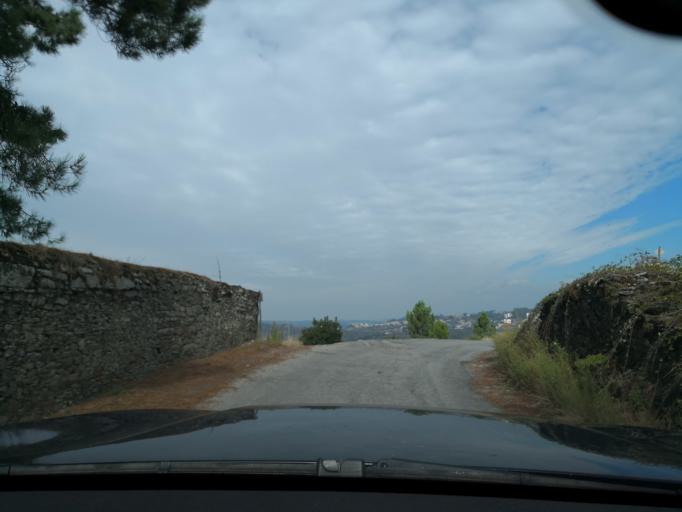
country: PT
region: Vila Real
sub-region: Peso da Regua
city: Peso da Regua
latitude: 41.2040
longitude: -7.7010
